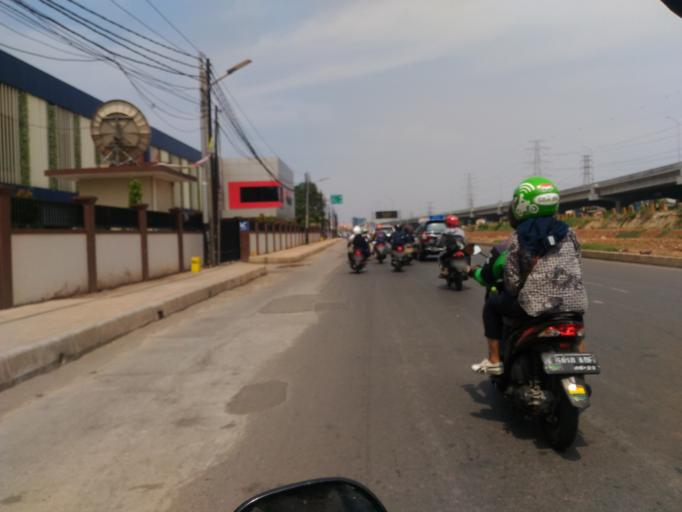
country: ID
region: Jakarta Raya
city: Jakarta
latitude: -6.2397
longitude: 106.8813
